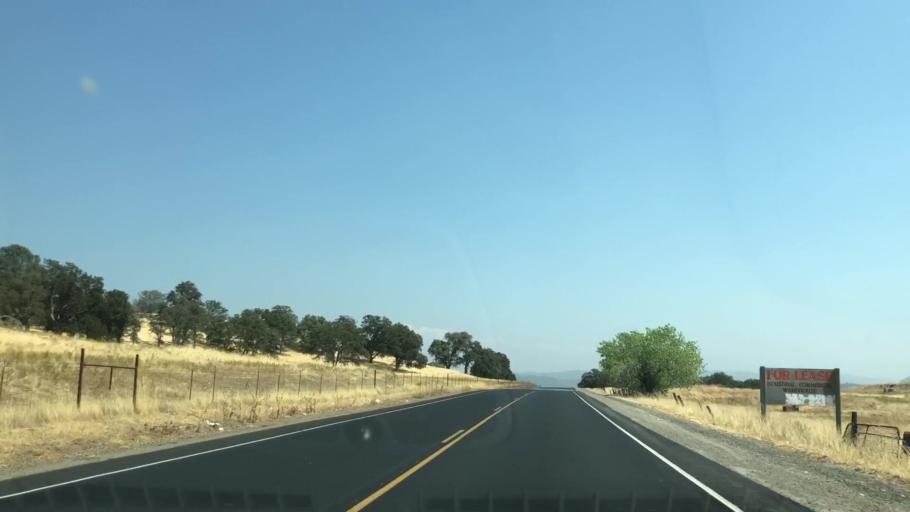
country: US
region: California
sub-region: Tuolumne County
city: Jamestown
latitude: 37.8802
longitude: -120.4679
